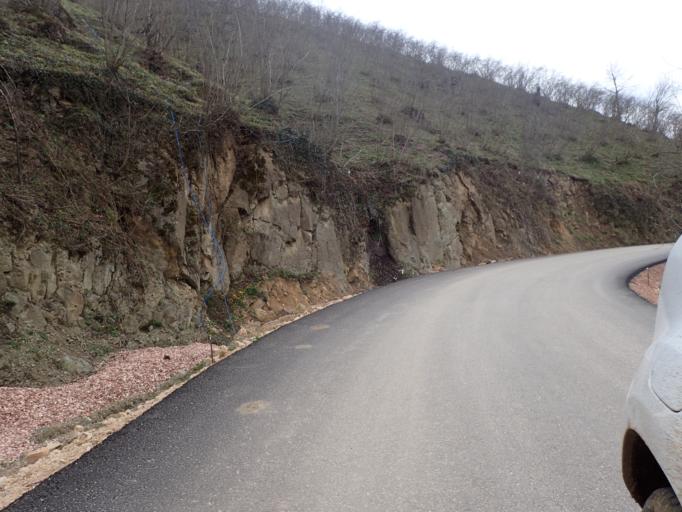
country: TR
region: Ordu
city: Camas
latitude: 40.8895
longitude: 37.5150
